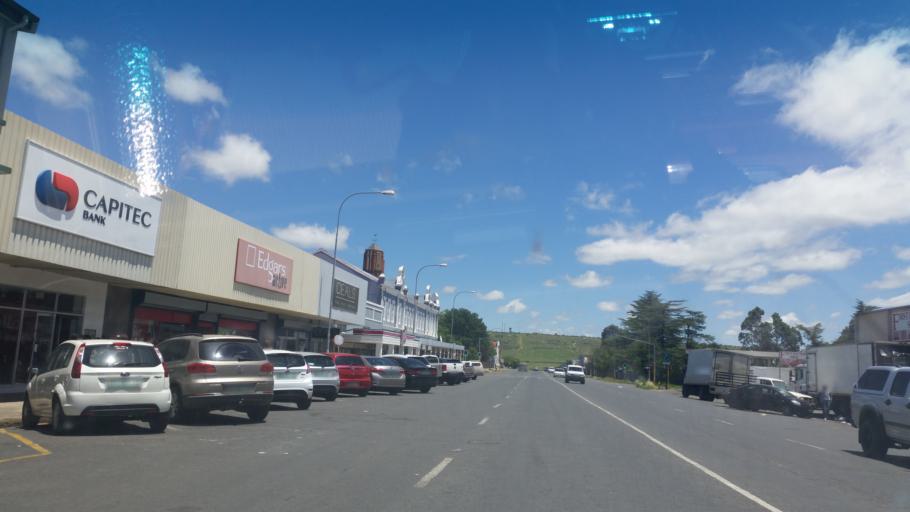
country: ZA
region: Orange Free State
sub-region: Thabo Mofutsanyana District Municipality
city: Harrismith
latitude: -28.2693
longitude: 29.1242
